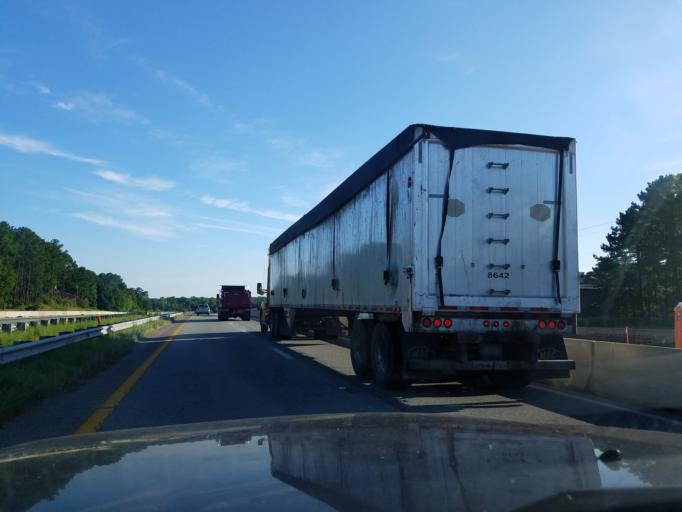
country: US
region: North Carolina
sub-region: Durham County
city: Durham
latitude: 35.9971
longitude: -78.8630
